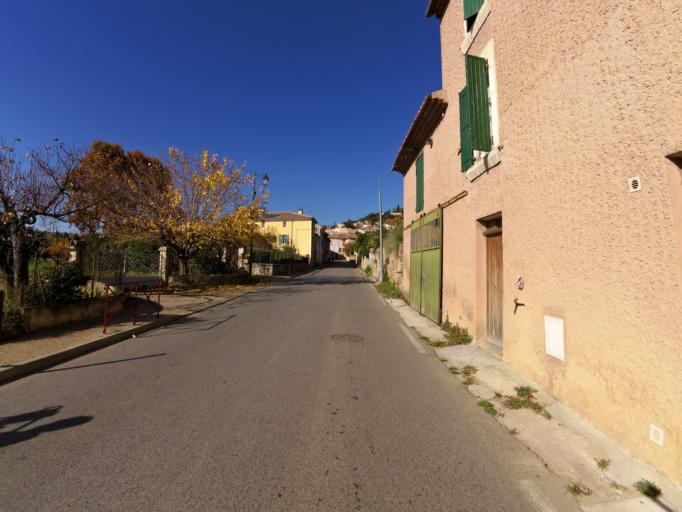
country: FR
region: Provence-Alpes-Cote d'Azur
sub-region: Departement du Vaucluse
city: Bedoin
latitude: 44.1210
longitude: 5.1787
